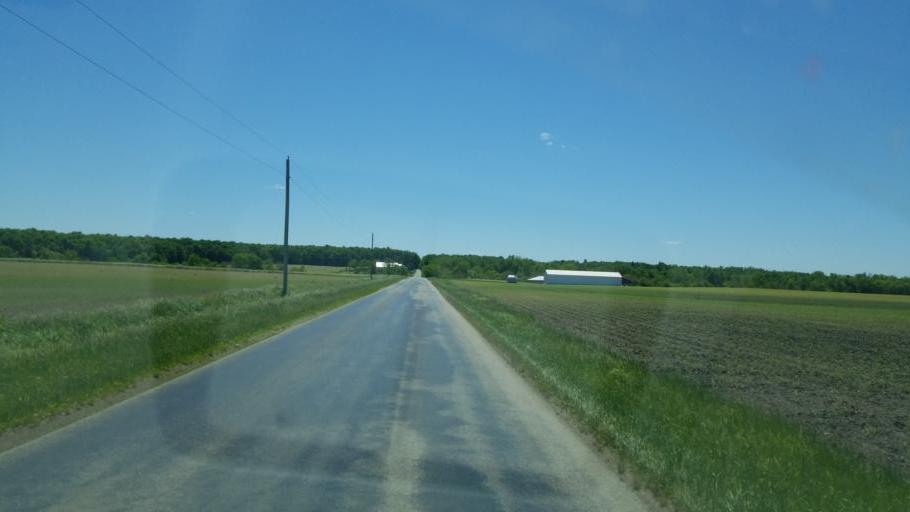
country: US
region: Ohio
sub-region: Mercer County
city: Fort Recovery
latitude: 40.3334
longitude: -84.8037
